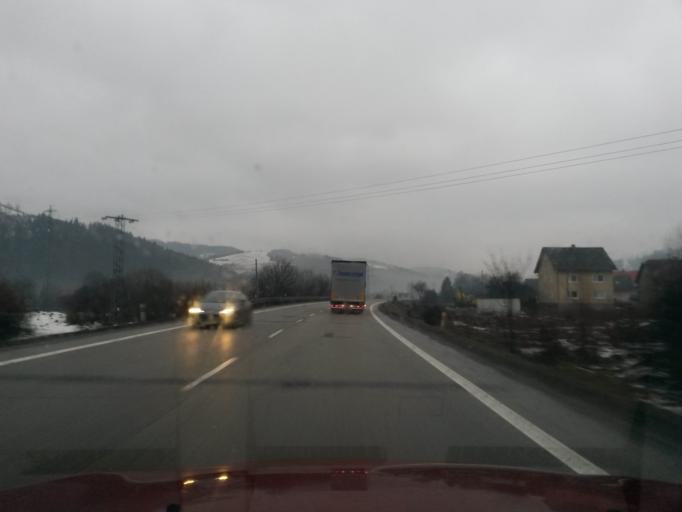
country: SK
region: Zilinsky
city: Kysucke Nove Mesto
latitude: 49.3335
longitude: 18.8082
